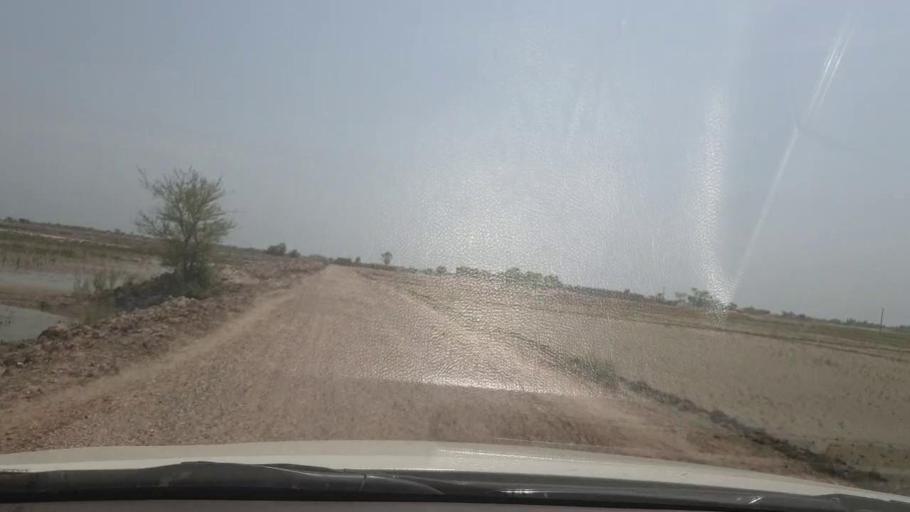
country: PK
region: Sindh
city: Shikarpur
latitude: 28.0304
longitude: 68.5715
